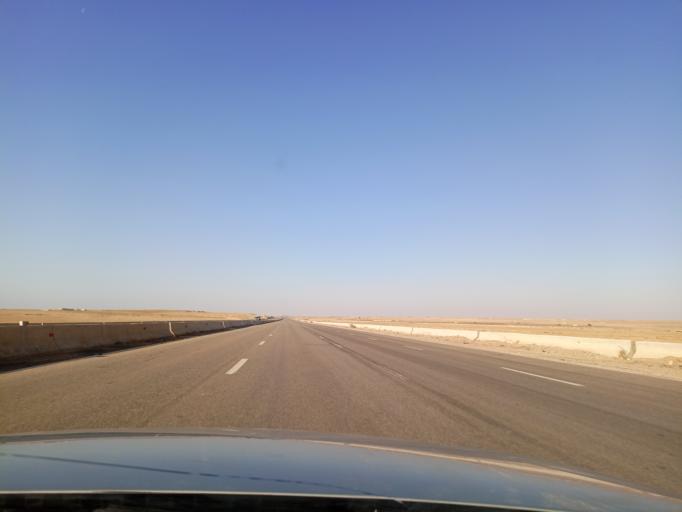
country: EG
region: Muhafazat al Fayyum
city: Tamiyah
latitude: 29.6111
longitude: 30.9192
